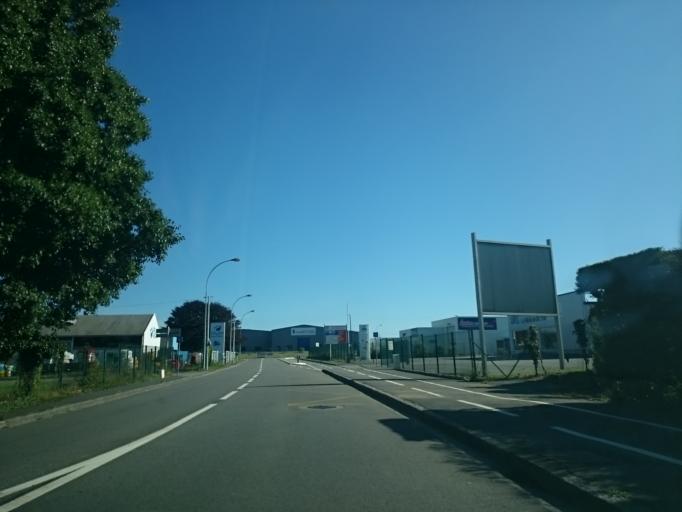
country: FR
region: Brittany
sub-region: Departement du Finistere
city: Gouesnou
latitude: 48.4242
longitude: -4.4604
